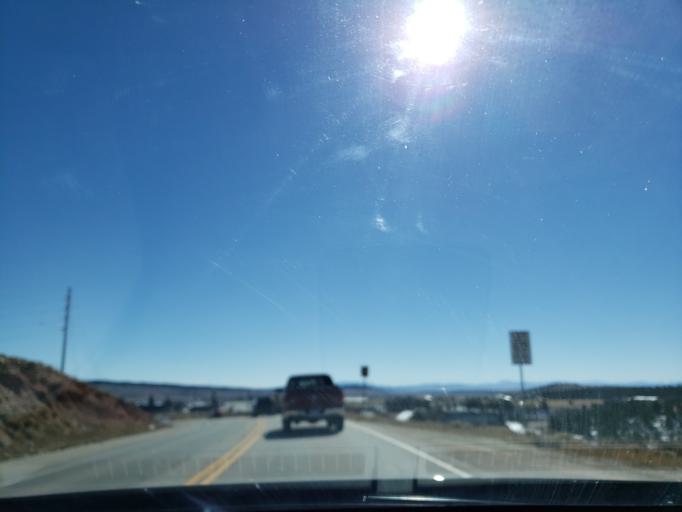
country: US
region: Colorado
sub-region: Park County
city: Fairplay
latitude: 39.2265
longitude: -106.0063
